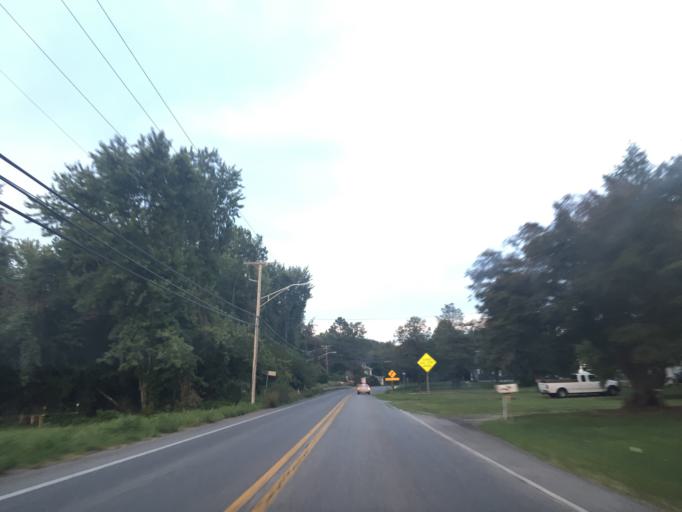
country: US
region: Maryland
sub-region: Anne Arundel County
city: Gambrills
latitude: 39.0653
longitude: -76.6656
